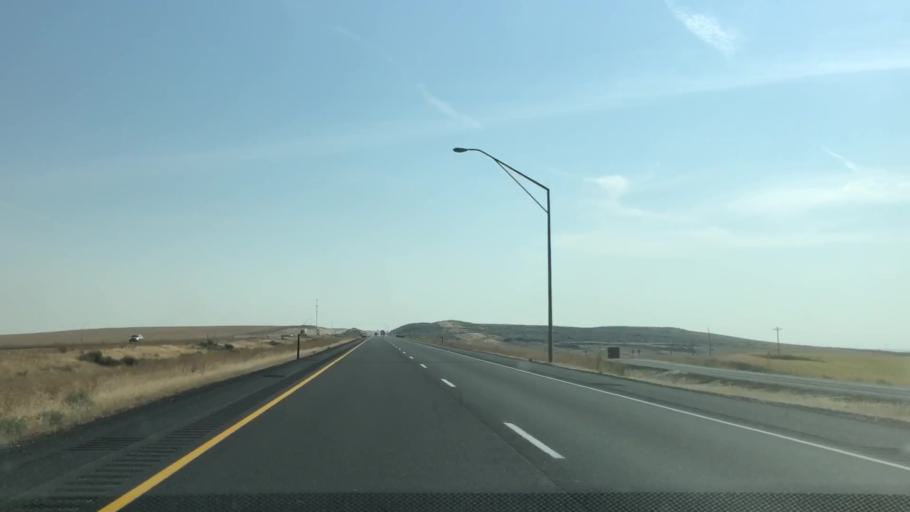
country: US
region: Washington
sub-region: Grant County
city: Warden
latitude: 47.0858
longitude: -118.8784
